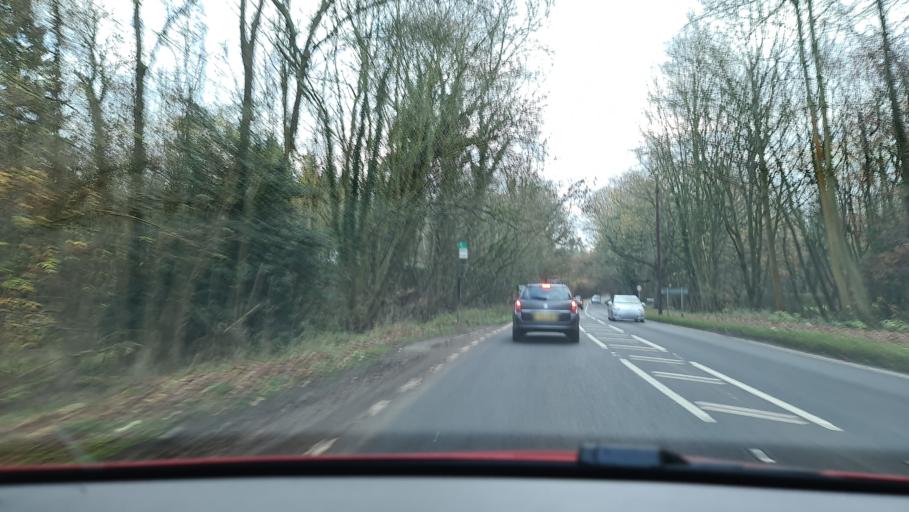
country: GB
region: England
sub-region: Buckinghamshire
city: Amersham
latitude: 51.6610
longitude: -0.6653
